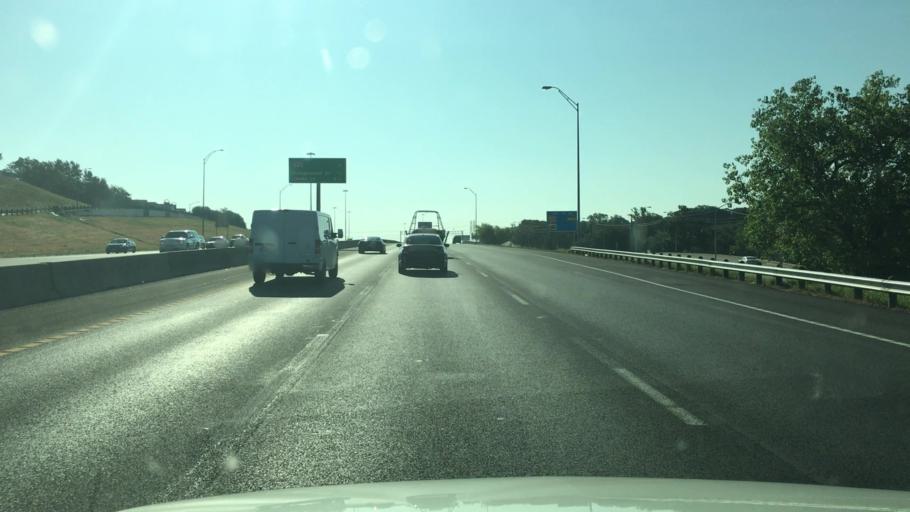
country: US
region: Texas
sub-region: Tarrant County
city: Haltom City
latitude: 32.7602
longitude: -97.2305
